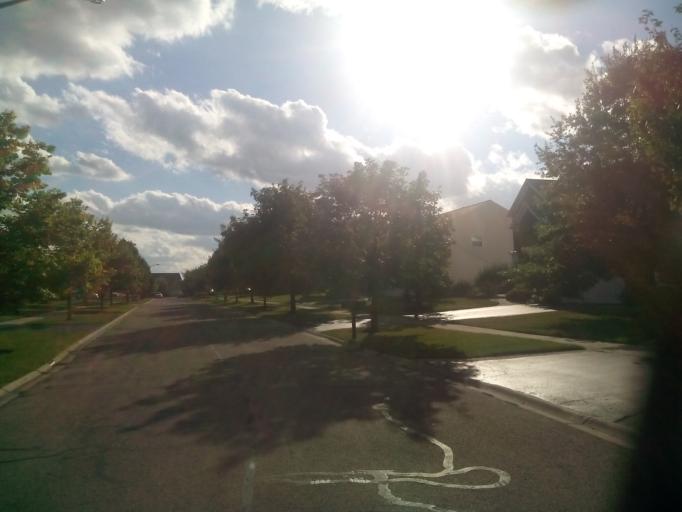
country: US
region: Illinois
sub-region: Will County
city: Bolingbrook
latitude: 41.7040
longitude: -88.1369
